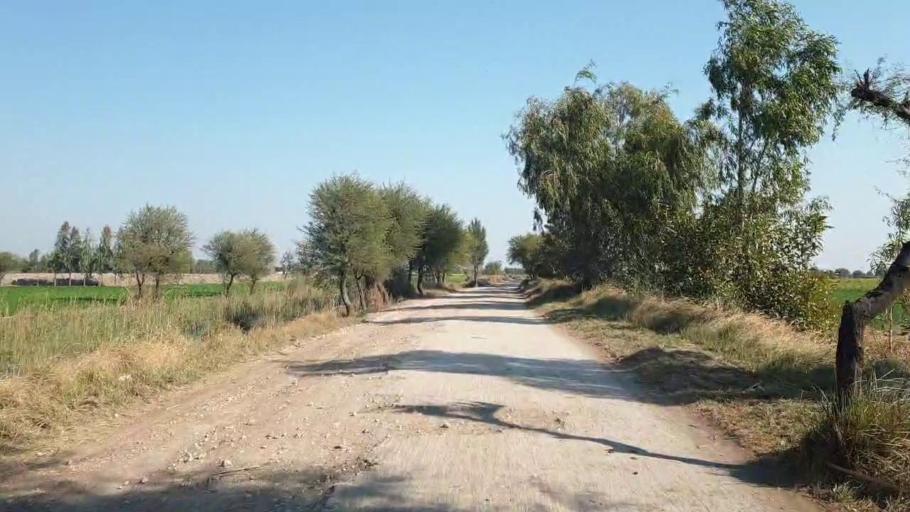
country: PK
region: Sindh
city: Shahdadpur
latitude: 25.9789
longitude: 68.6727
